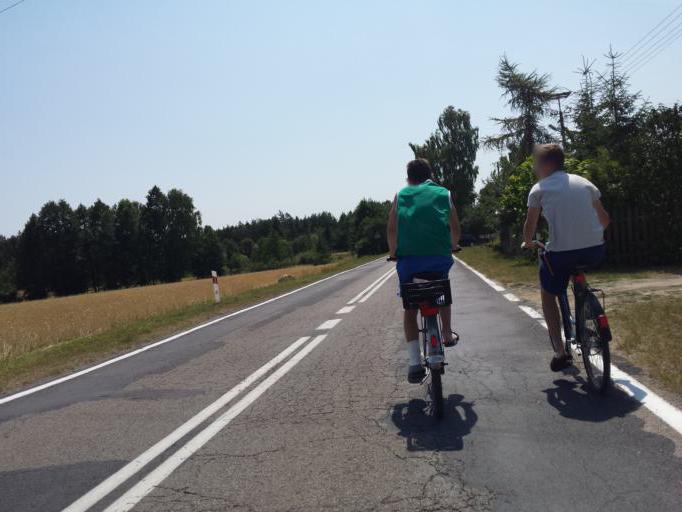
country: PL
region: Lublin Voivodeship
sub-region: Powiat bialski
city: Koden
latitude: 51.8977
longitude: 23.5977
